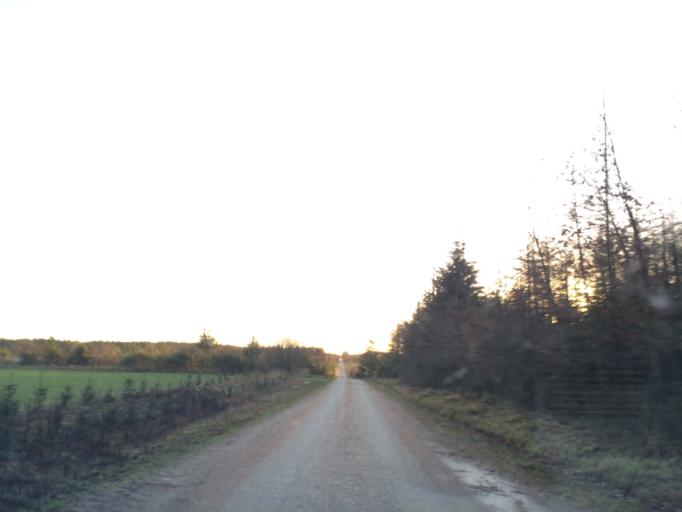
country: DK
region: Central Jutland
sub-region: Holstebro Kommune
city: Holstebro
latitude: 56.2238
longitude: 8.5016
